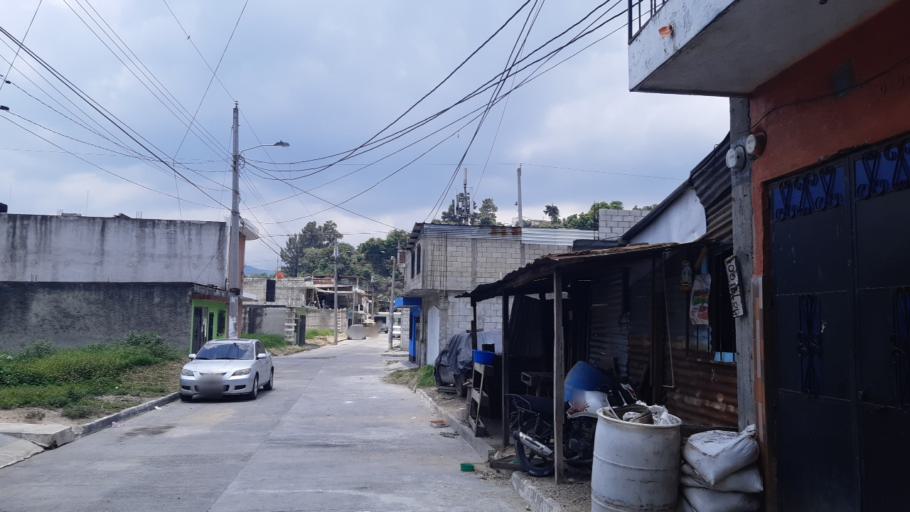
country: GT
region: Guatemala
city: Petapa
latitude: 14.5106
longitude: -90.5598
